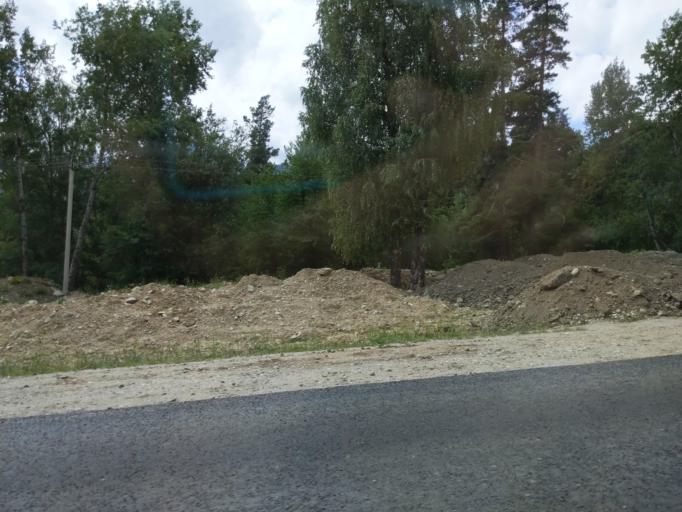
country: RU
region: Karachayevo-Cherkesiya
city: Nizhniy Arkhyz
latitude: 43.5372
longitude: 41.2145
